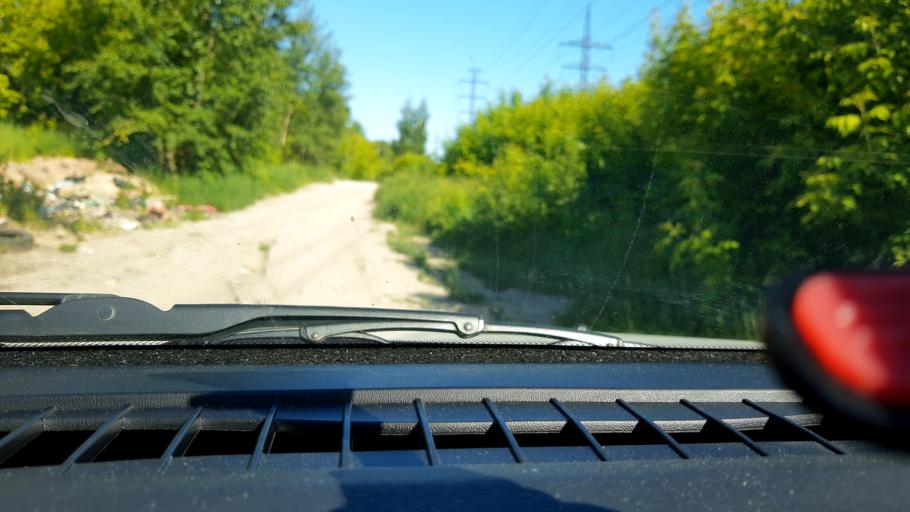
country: RU
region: Nizjnij Novgorod
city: Gorbatovka
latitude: 56.3513
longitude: 43.8301
